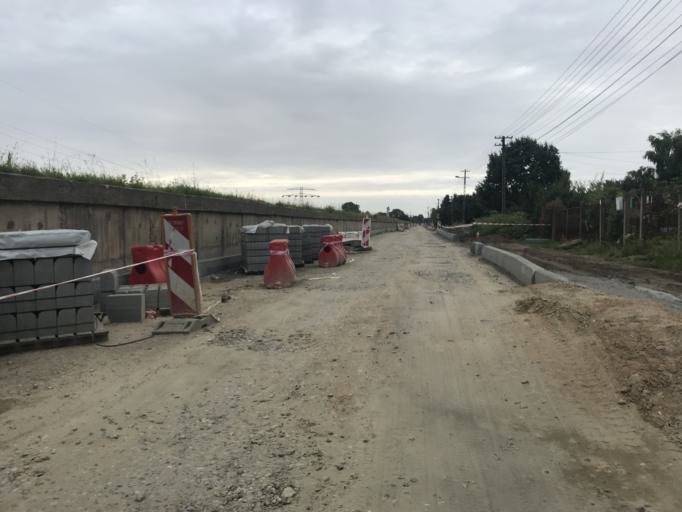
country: PL
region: Pomeranian Voivodeship
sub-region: Gdansk
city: Gdansk
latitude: 54.3440
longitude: 18.6818
